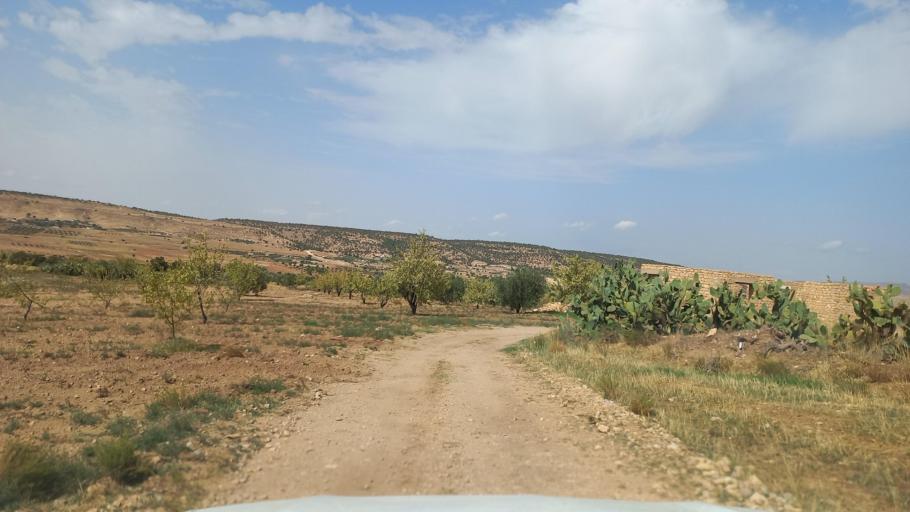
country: TN
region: Al Qasrayn
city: Kasserine
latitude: 35.3540
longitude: 8.8905
